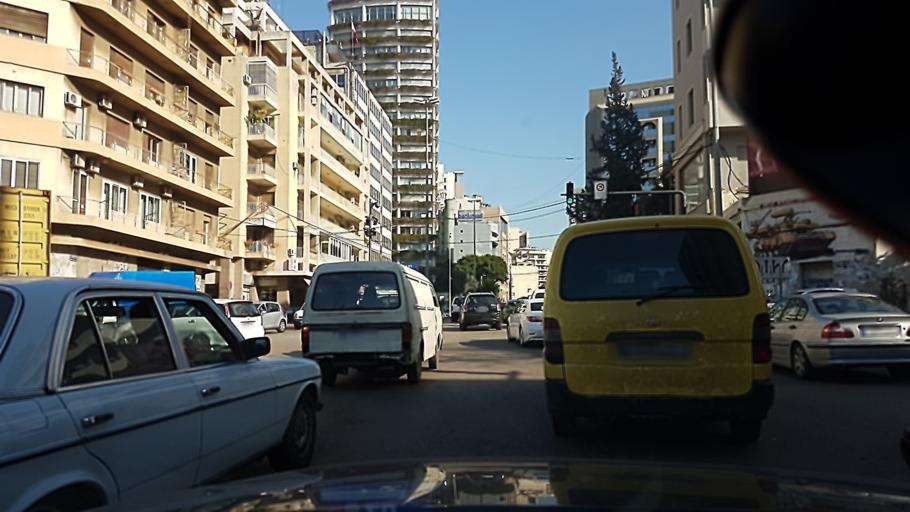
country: LB
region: Beyrouth
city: Beirut
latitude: 33.8923
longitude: 35.5097
